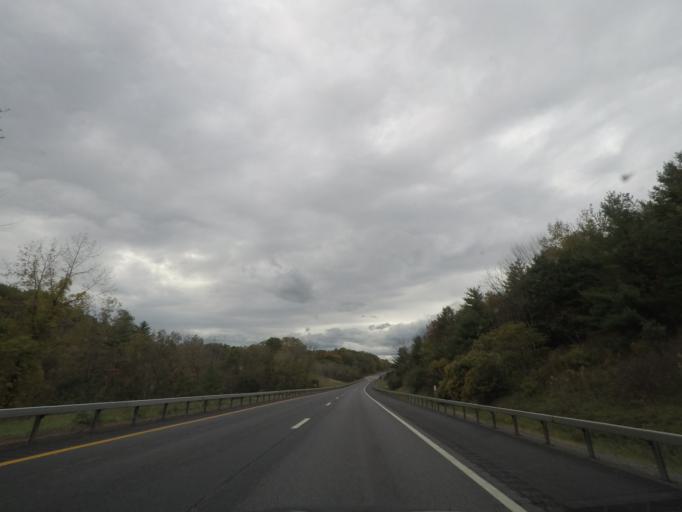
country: US
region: New York
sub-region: Rensselaer County
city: Castleton-on-Hudson
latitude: 42.4967
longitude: -73.7264
